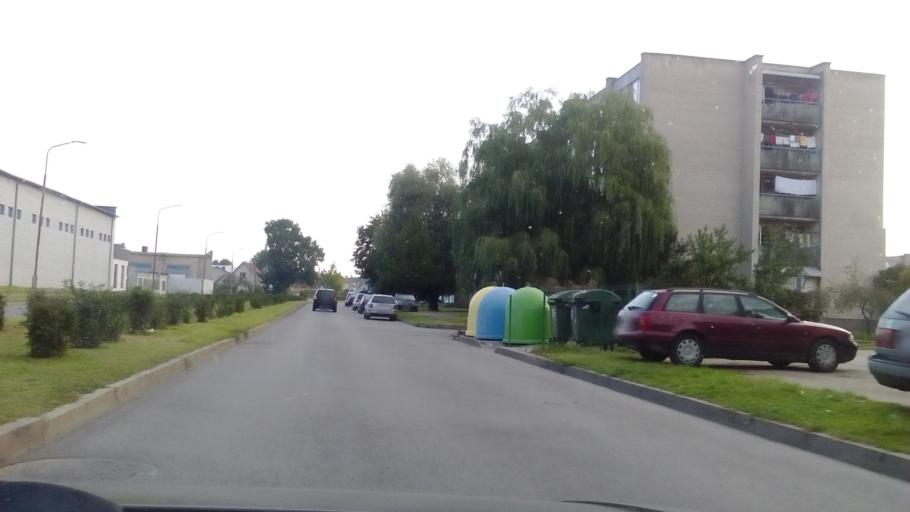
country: LT
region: Alytaus apskritis
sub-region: Alytus
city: Alytus
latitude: 54.3837
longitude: 24.0557
